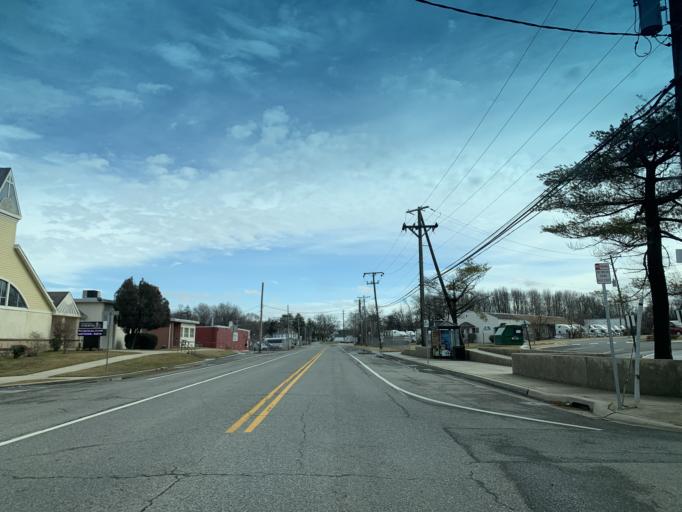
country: US
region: Delaware
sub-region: New Castle County
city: Wilmington
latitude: 39.7131
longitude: -75.5499
